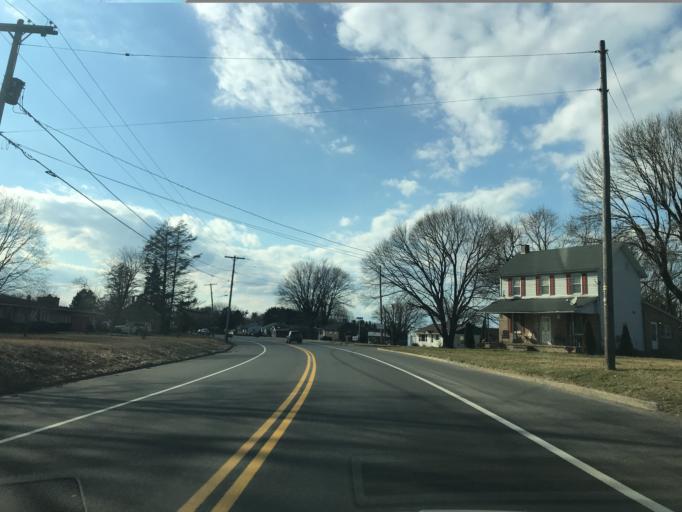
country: US
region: Maryland
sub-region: Cecil County
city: Rising Sun
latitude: 39.6894
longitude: -76.0412
